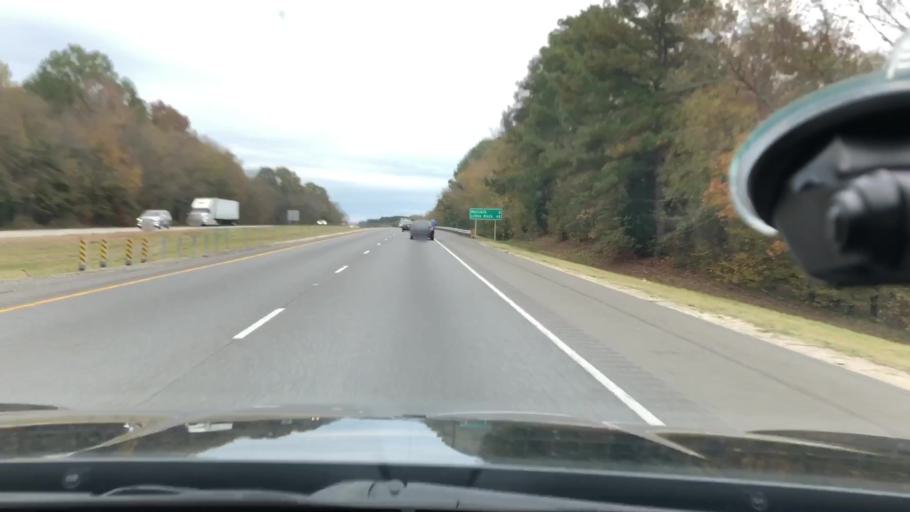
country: US
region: Arkansas
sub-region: Hot Spring County
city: Malvern
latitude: 34.3425
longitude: -92.9064
